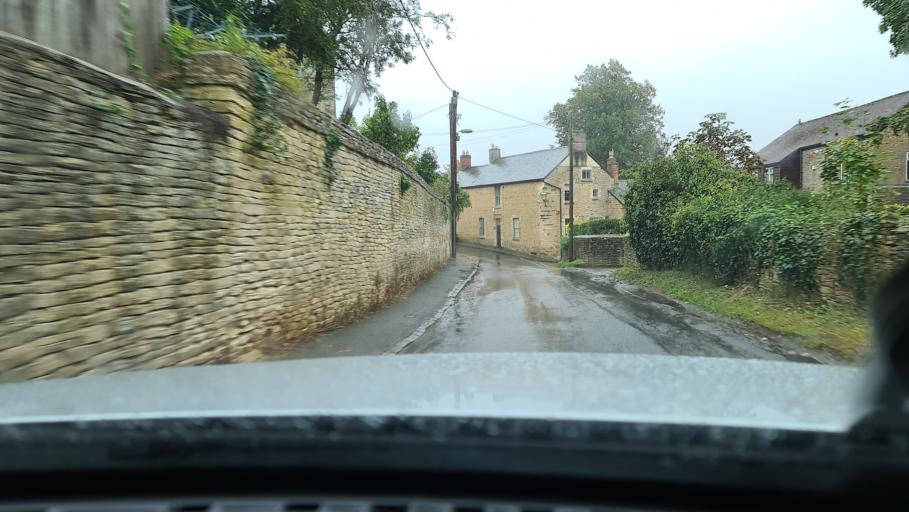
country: GB
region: England
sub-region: Oxfordshire
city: Somerton
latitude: 51.9313
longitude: -1.3146
